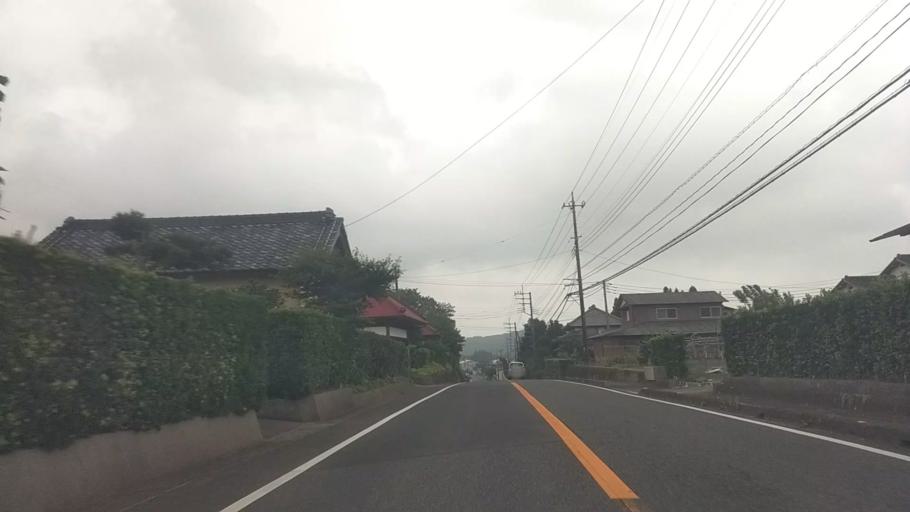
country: JP
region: Chiba
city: Ohara
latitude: 35.2820
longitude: 140.2930
